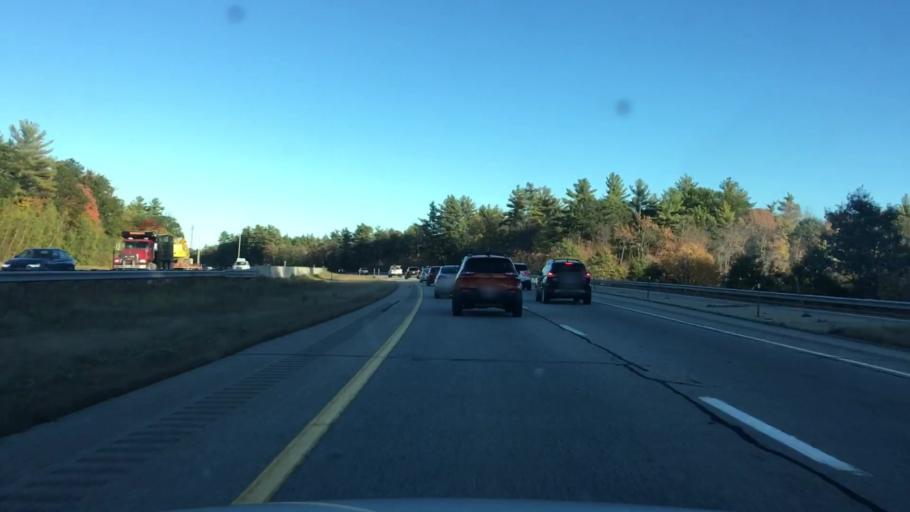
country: US
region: New Hampshire
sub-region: Rockingham County
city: Epping
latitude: 43.0259
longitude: -71.1136
